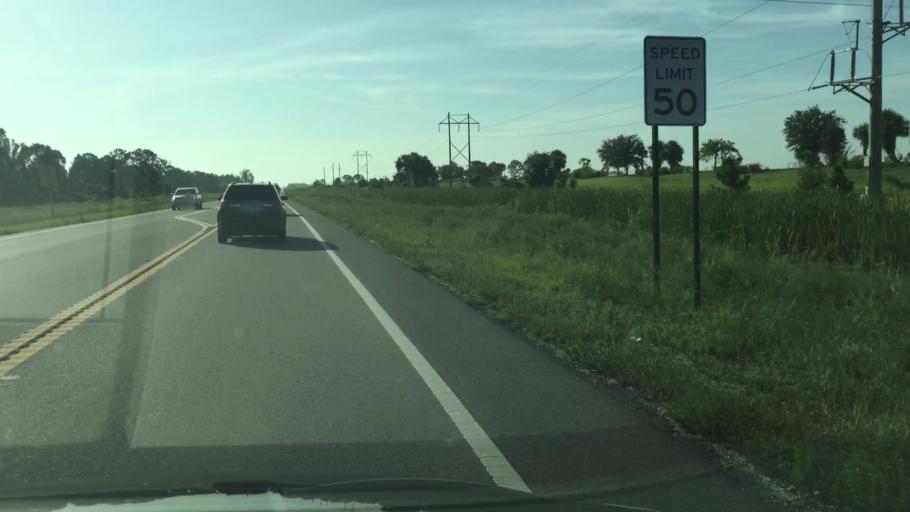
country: US
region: Florida
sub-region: Lee County
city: Lehigh Acres
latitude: 26.5284
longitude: -81.6038
